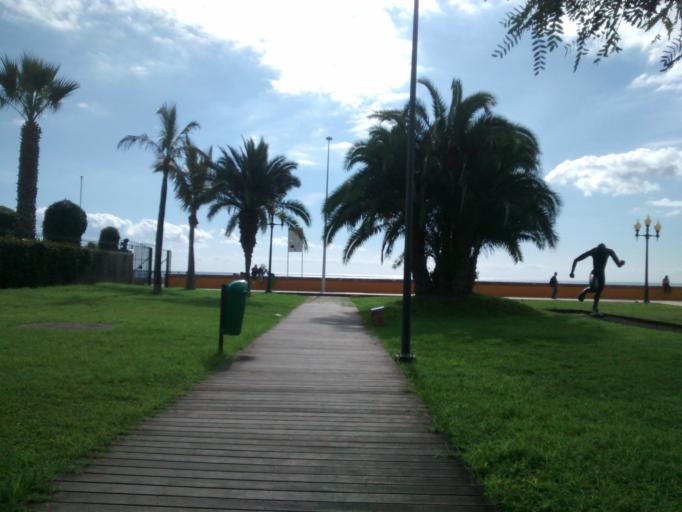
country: PT
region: Madeira
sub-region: Funchal
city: Funchal
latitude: 32.6472
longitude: -16.9010
